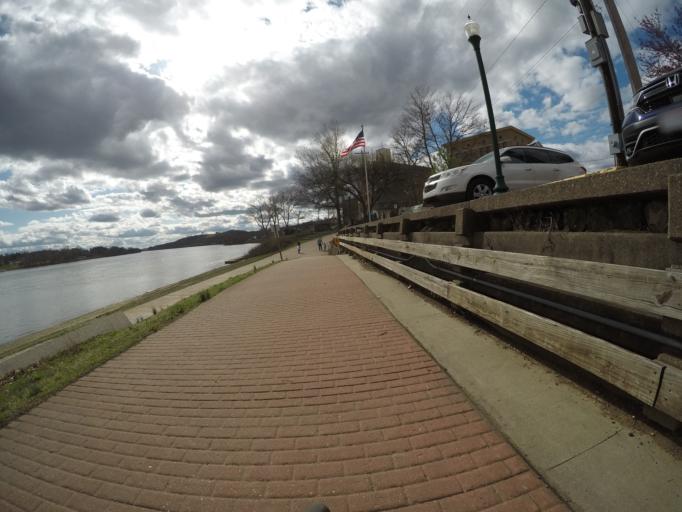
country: US
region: Ohio
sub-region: Washington County
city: Marietta
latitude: 39.4106
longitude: -81.4511
